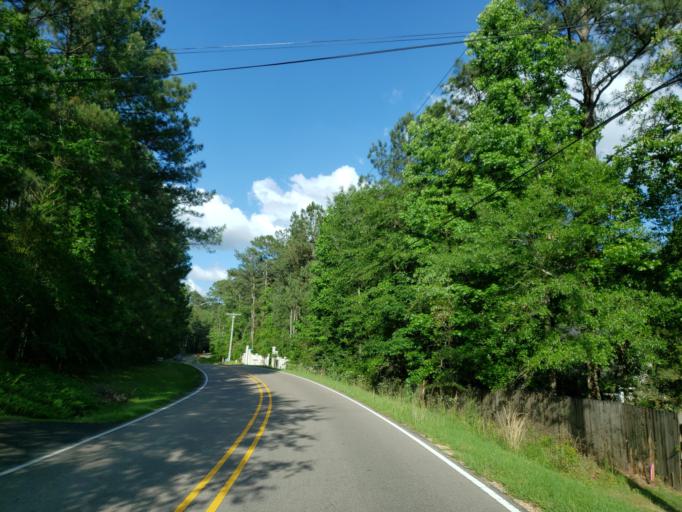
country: US
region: Mississippi
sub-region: Lamar County
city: West Hattiesburg
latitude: 31.2721
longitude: -89.4052
